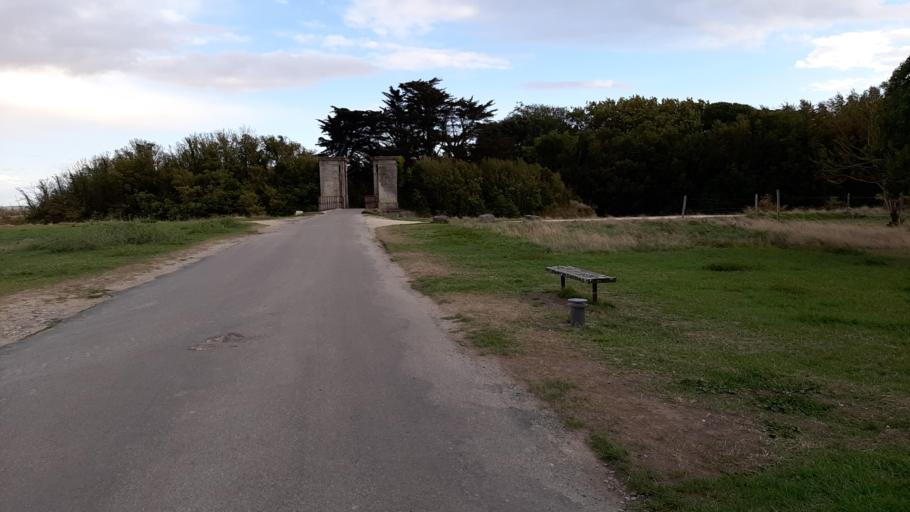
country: FR
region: Poitou-Charentes
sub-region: Departement de la Charente-Maritime
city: Boyard-Ville
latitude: 46.0139
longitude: -1.1732
